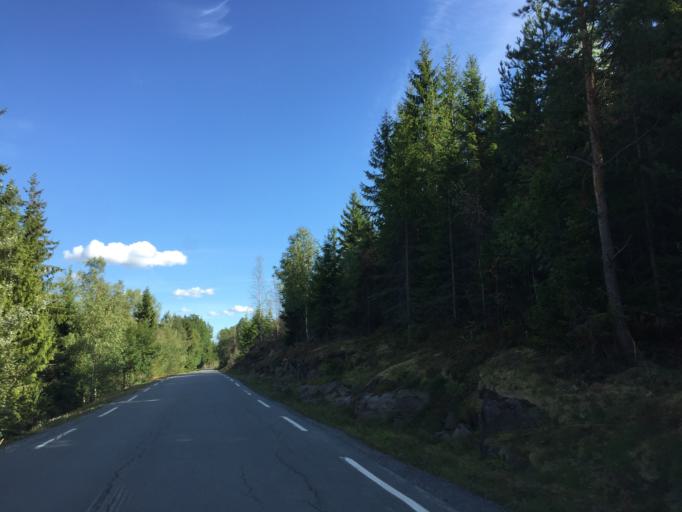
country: NO
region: Buskerud
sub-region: Ovre Eiker
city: Hokksund
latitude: 59.6614
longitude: 9.8976
